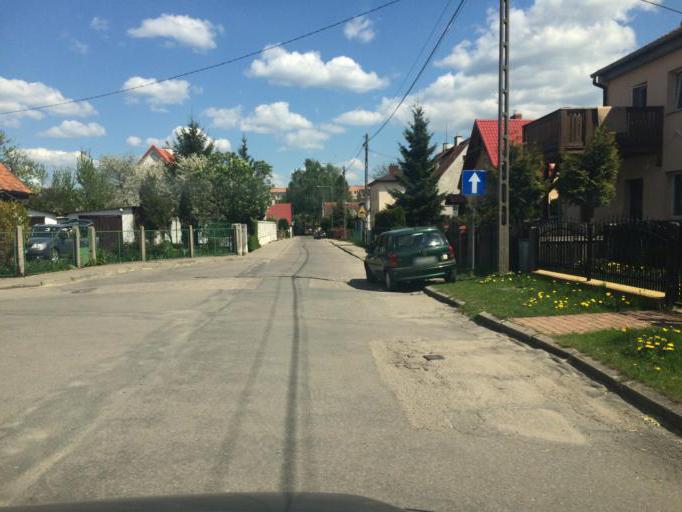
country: PL
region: Warmian-Masurian Voivodeship
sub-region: Powiat ostrodzki
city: Ostroda
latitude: 53.6896
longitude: 19.9659
